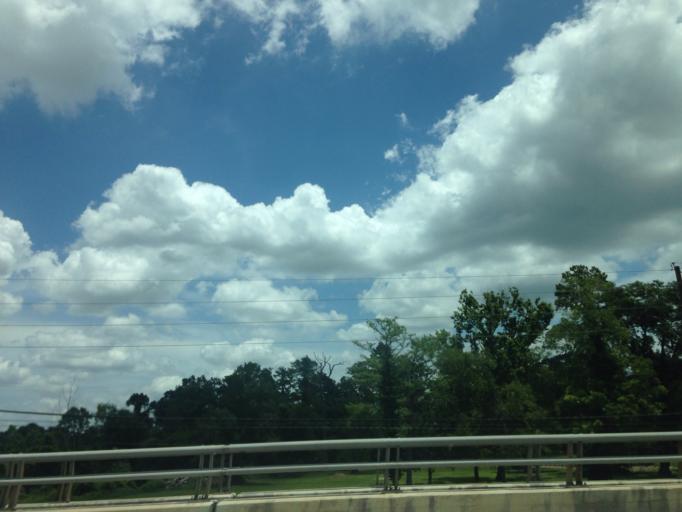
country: US
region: Texas
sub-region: Harris County
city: Spring
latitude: 30.0241
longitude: -95.4762
